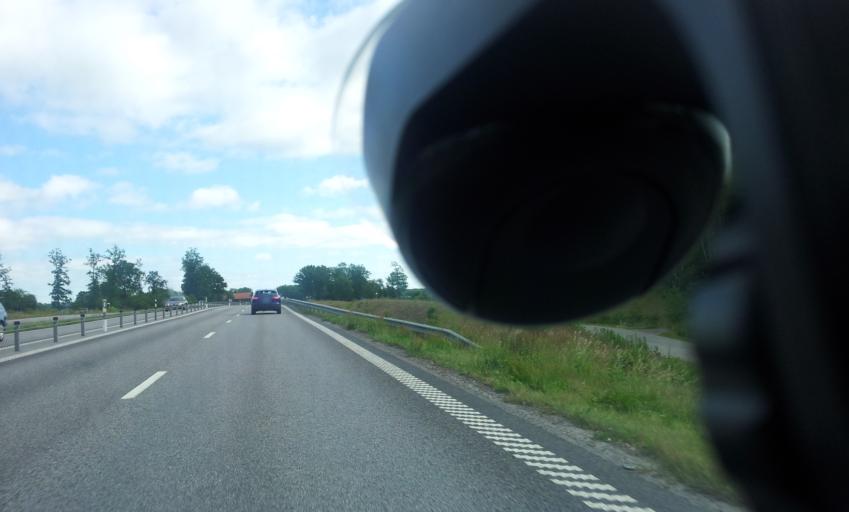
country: SE
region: Kalmar
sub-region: Kalmar Kommun
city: Lindsdal
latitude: 56.7697
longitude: 16.3248
